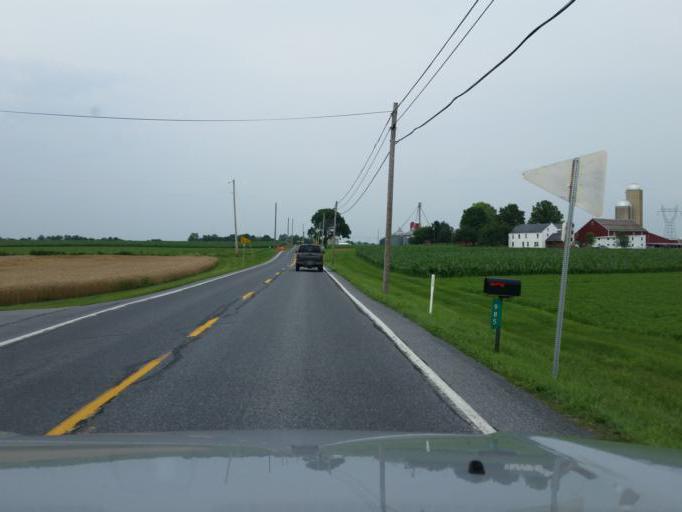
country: US
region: Pennsylvania
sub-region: Lancaster County
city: Manheim
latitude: 40.1587
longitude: -76.3586
